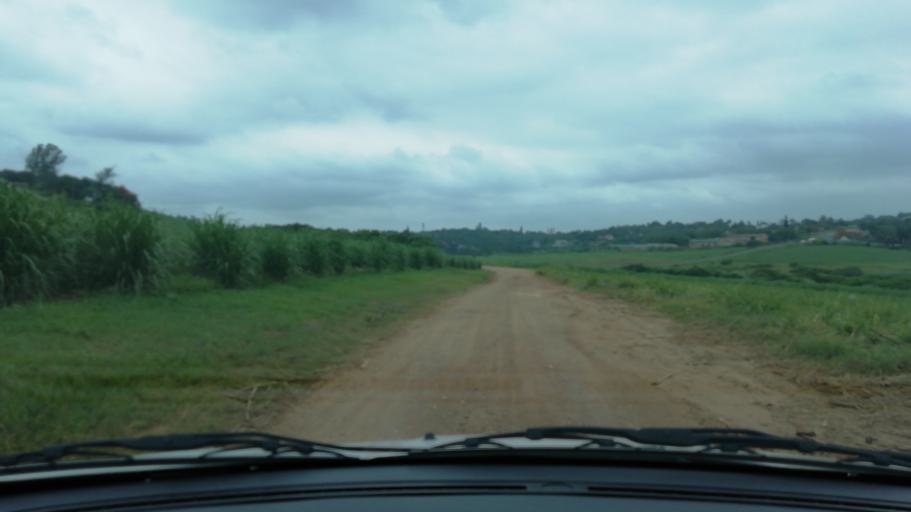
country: ZA
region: KwaZulu-Natal
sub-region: uThungulu District Municipality
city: Empangeni
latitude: -28.7355
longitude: 31.9078
